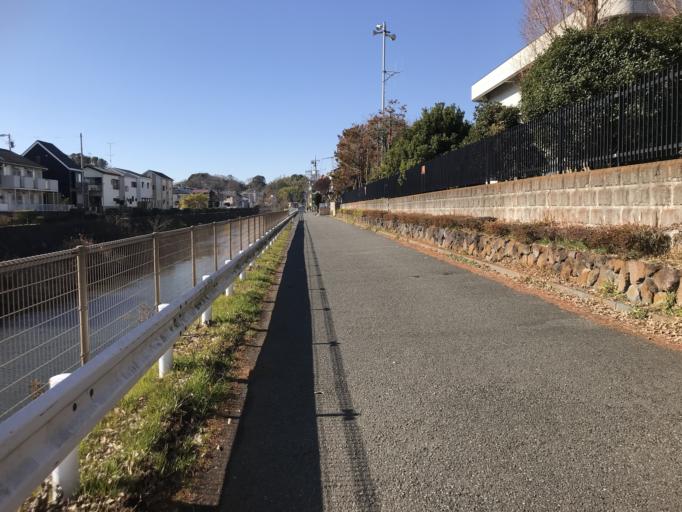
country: JP
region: Tokyo
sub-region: Machida-shi
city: Machida
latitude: 35.5777
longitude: 139.5022
